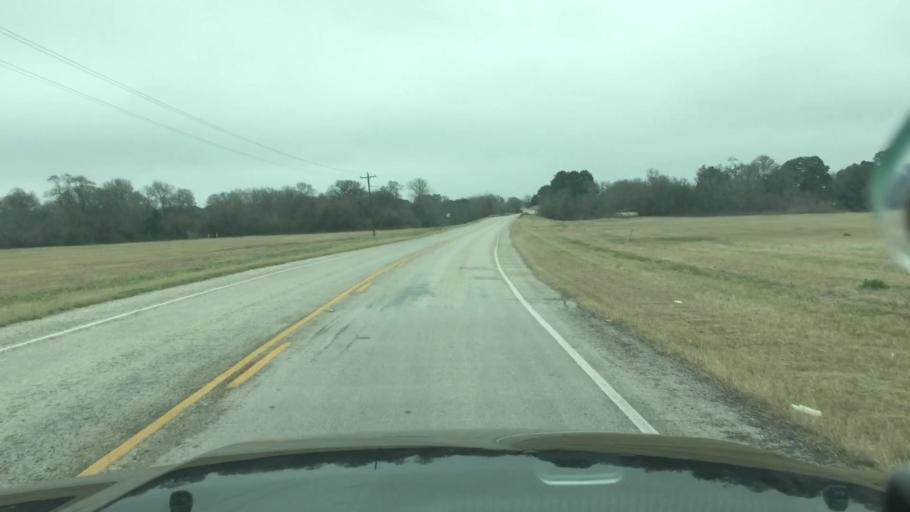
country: US
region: Texas
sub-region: Fayette County
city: La Grange
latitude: 30.0106
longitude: -96.9127
